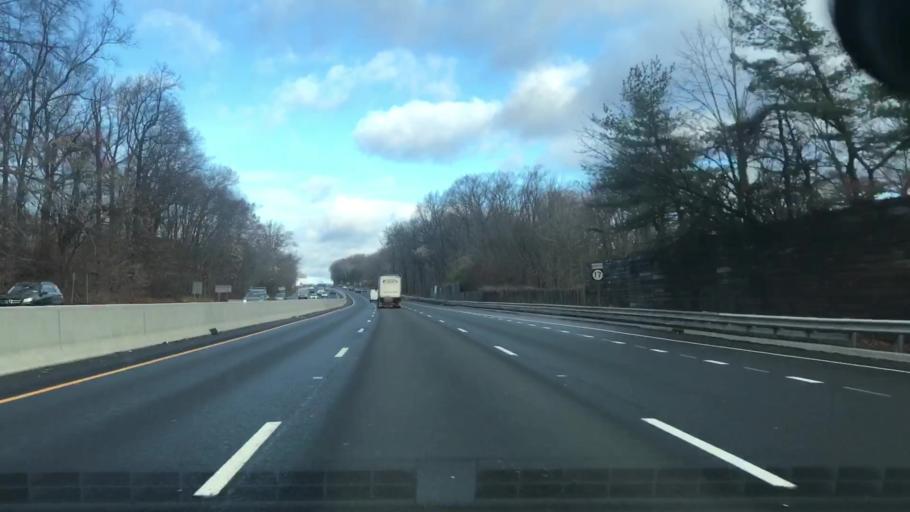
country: US
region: New Jersey
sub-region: Bergen County
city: Saddle River
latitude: 41.0349
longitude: -74.1118
